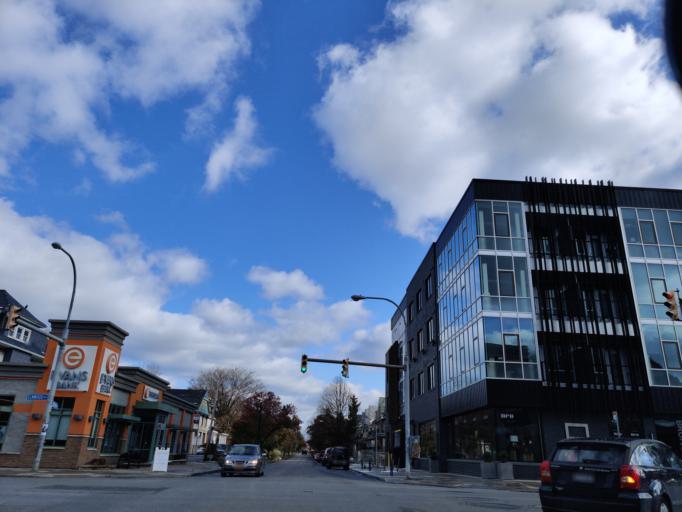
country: US
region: New York
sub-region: Erie County
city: Buffalo
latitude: 42.9222
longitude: -78.8772
